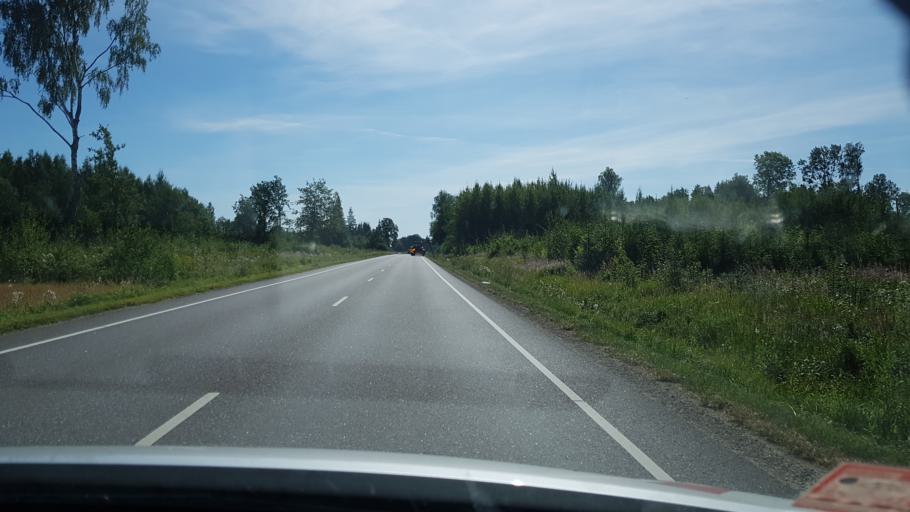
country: EE
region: Tartu
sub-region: Tartu linn
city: Tartu
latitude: 58.4400
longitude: 26.8225
